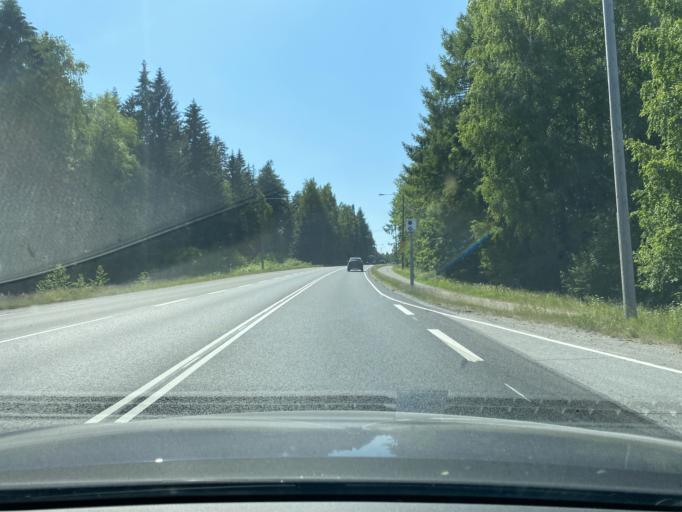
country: FI
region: Pirkanmaa
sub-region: Tampere
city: Nokia
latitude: 61.4684
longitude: 23.5216
